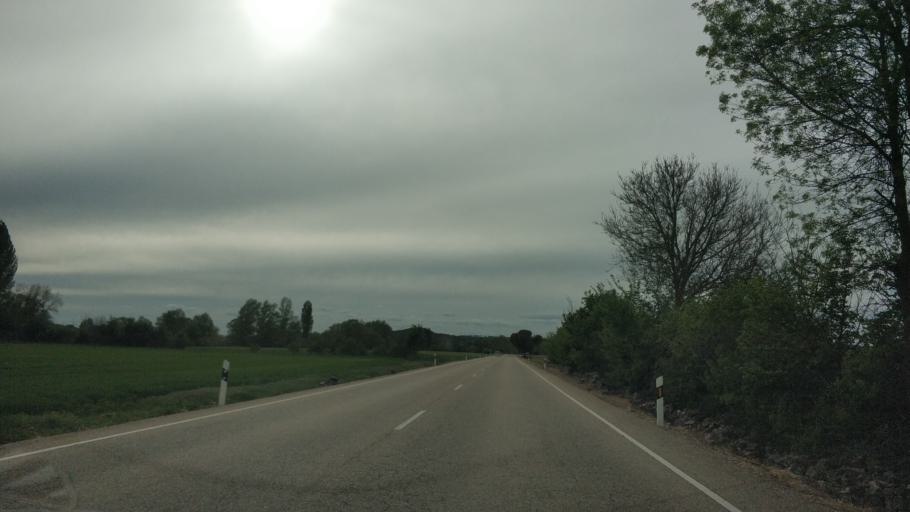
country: ES
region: Castille and Leon
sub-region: Provincia de Soria
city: Bayubas de Abajo
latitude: 41.4987
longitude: -2.8799
